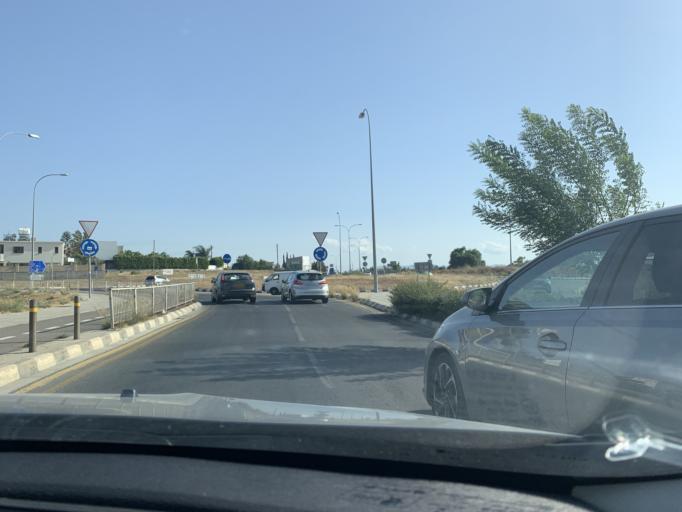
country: CY
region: Lefkosia
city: Tseri
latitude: 35.1160
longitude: 33.3562
